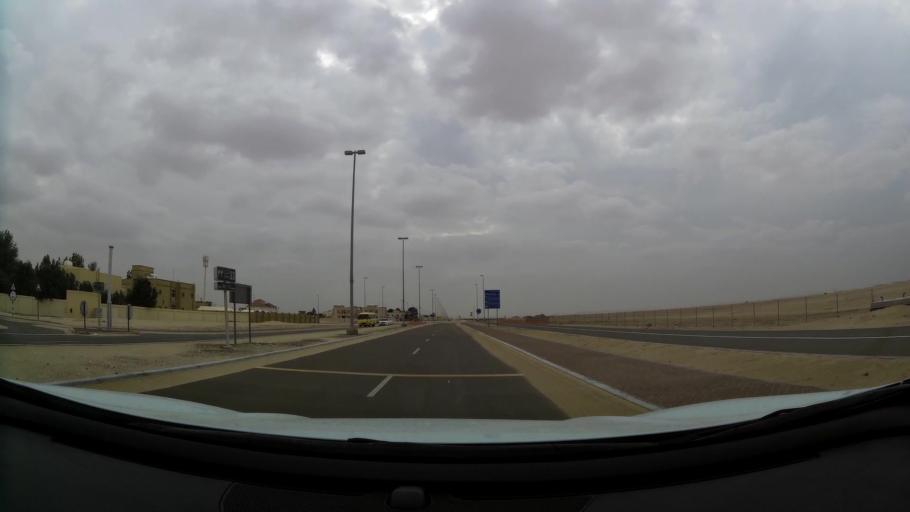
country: AE
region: Abu Dhabi
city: Abu Dhabi
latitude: 24.3779
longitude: 54.6308
